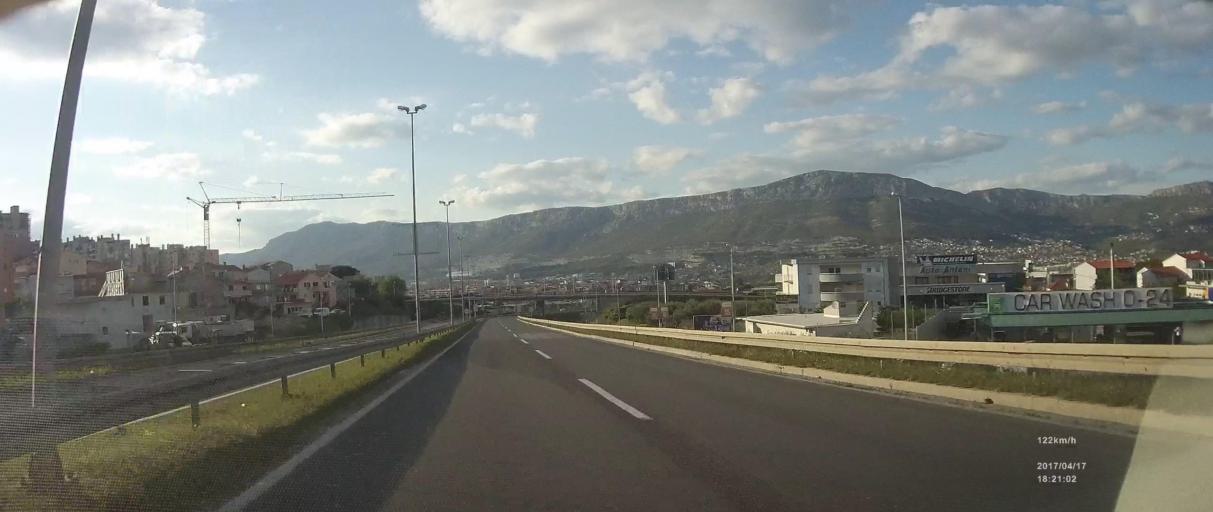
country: HR
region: Splitsko-Dalmatinska
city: Vranjic
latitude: 43.5142
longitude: 16.4827
